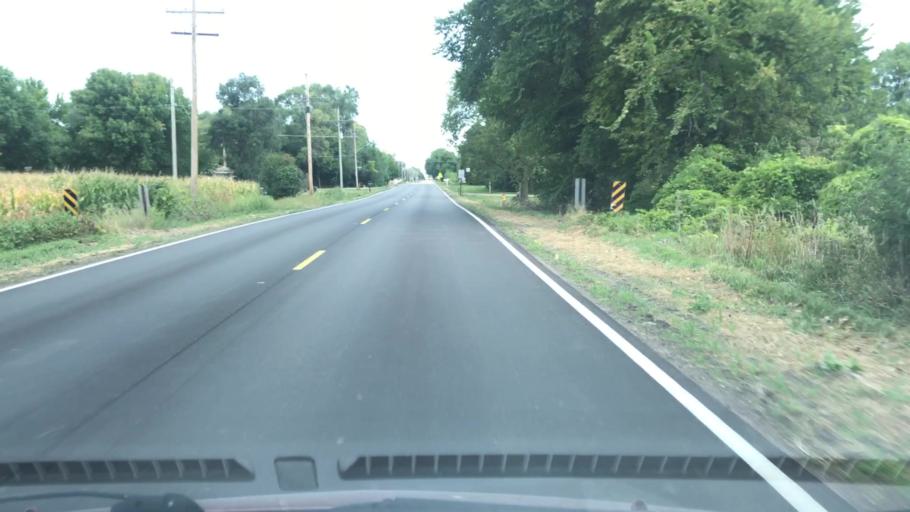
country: US
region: Nebraska
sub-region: Hall County
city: Grand Island
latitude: 40.9271
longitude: -98.3015
